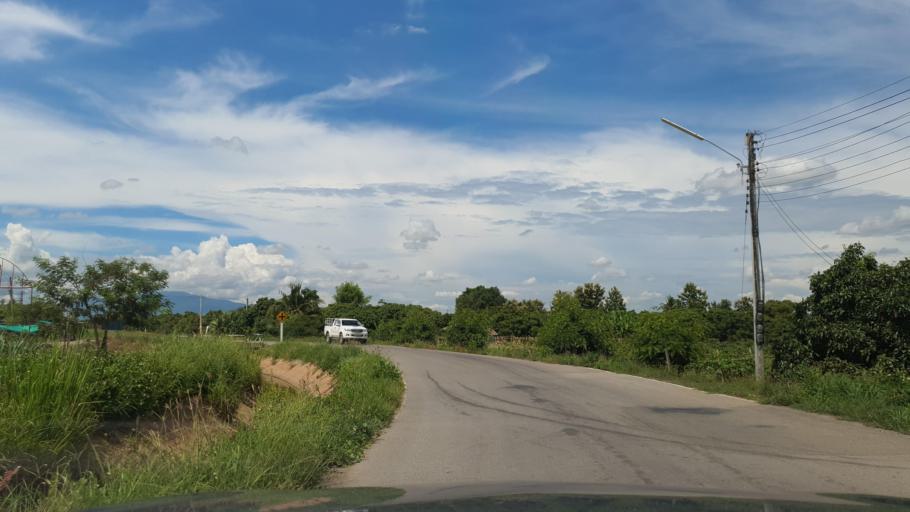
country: TH
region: Chiang Mai
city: San Pa Tong
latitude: 18.5904
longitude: 98.9056
